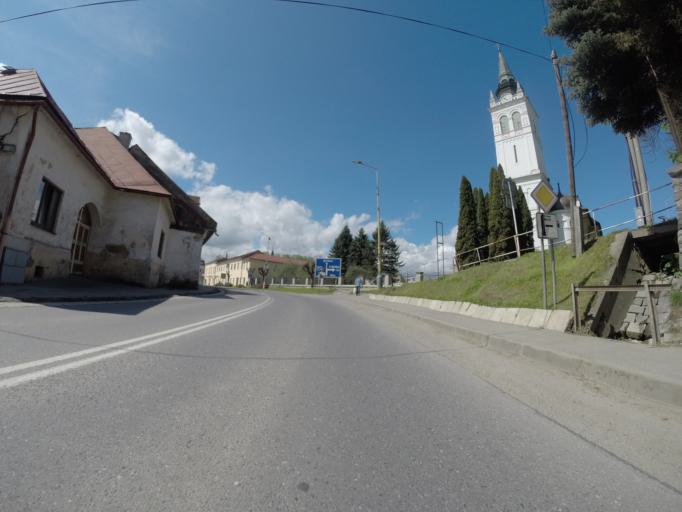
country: SK
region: Banskobystricky
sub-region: Okres Banska Bystrica
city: Brezno
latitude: 48.8087
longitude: 19.6459
